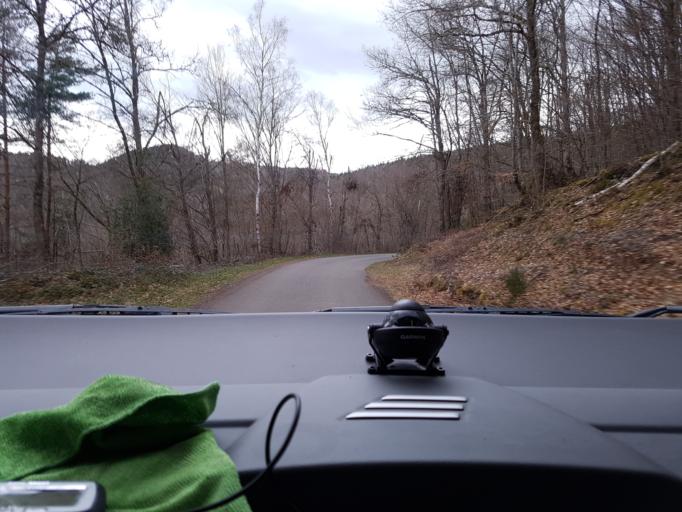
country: FR
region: Auvergne
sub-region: Departement du Puy-de-Dome
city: Chapdes-Beaufort
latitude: 45.8615
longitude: 2.8381
